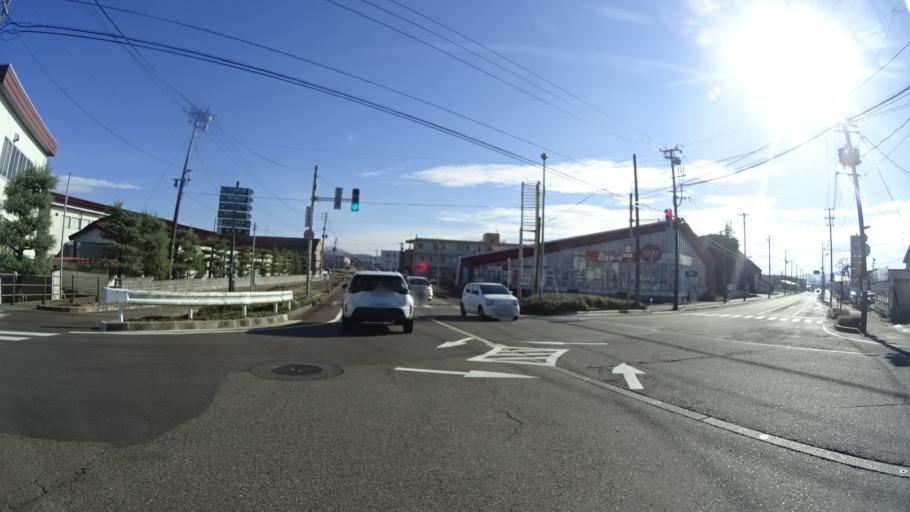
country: JP
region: Niigata
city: Mitsuke
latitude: 37.5372
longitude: 138.9044
